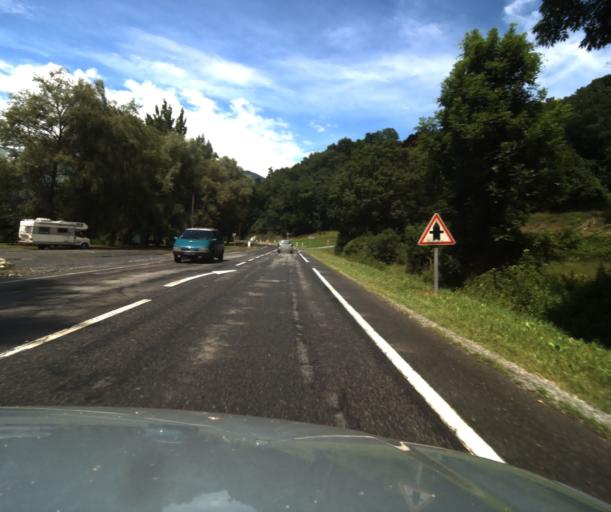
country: FR
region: Midi-Pyrenees
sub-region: Departement des Hautes-Pyrenees
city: Argeles-Gazost
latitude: 43.0030
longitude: -0.0791
